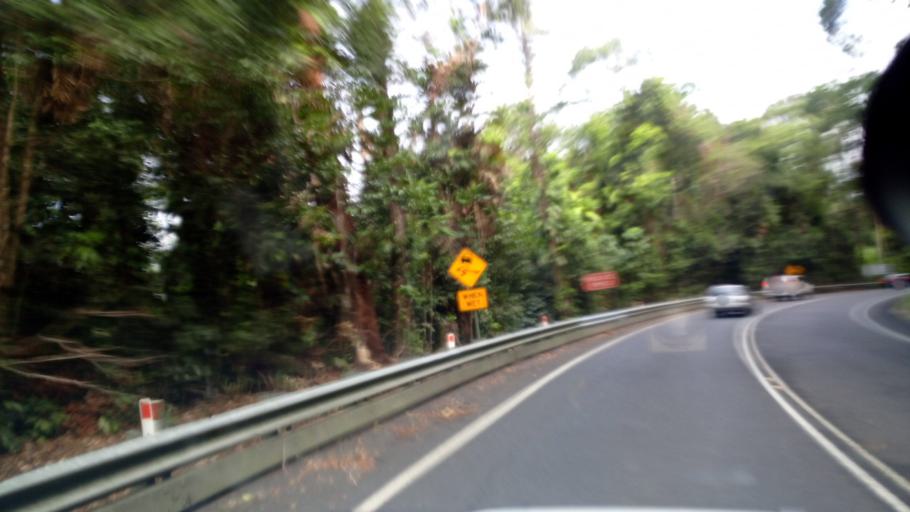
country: AU
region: Queensland
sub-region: Tablelands
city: Kuranda
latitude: -16.8207
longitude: 145.6467
